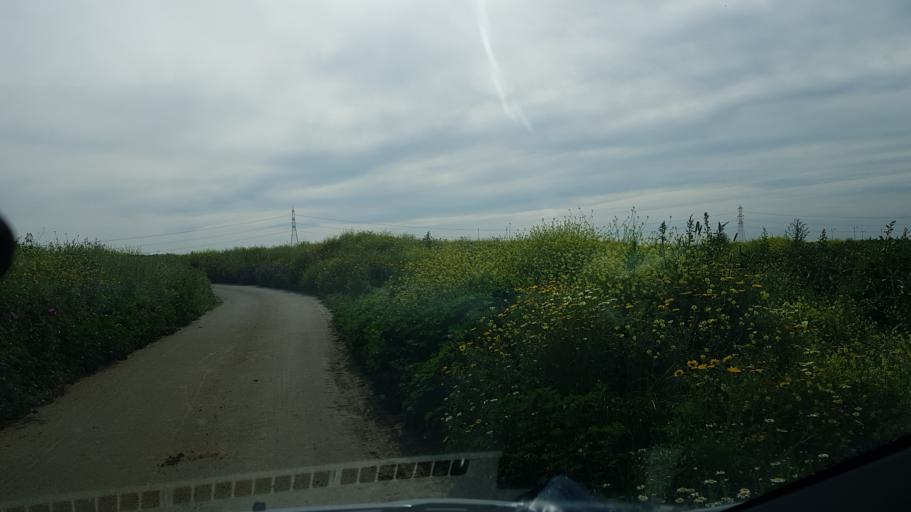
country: IT
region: Apulia
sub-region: Provincia di Brindisi
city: Tuturano
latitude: 40.5681
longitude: 17.9193
